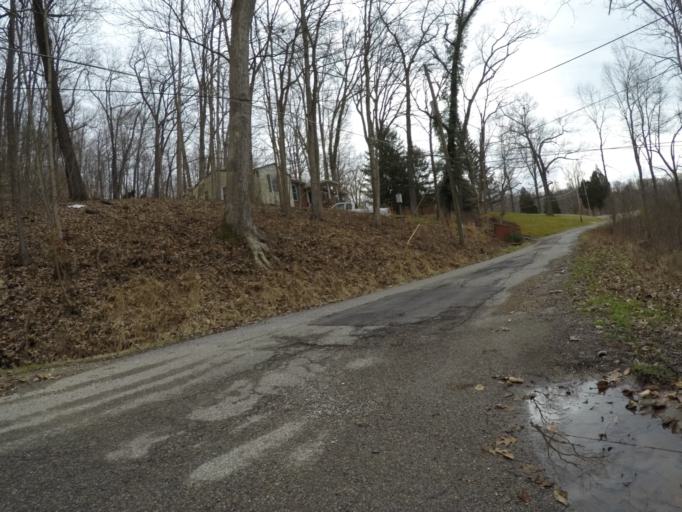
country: US
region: Ohio
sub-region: Lawrence County
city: Burlington
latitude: 38.3869
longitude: -82.5062
